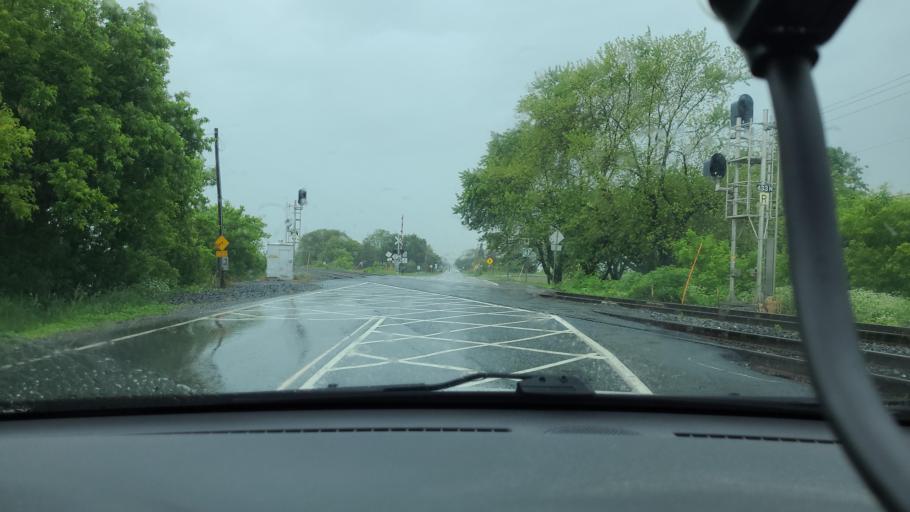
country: CA
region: Quebec
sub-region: Monteregie
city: Saint-Hyacinthe
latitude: 45.6175
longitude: -72.9952
